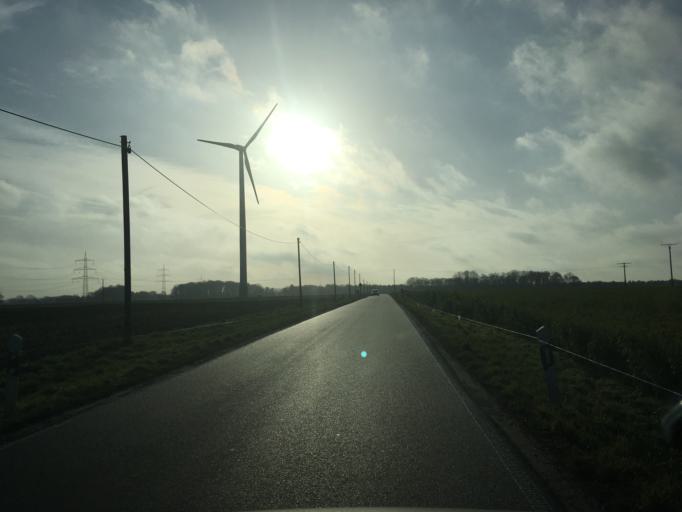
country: DE
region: North Rhine-Westphalia
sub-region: Regierungsbezirk Munster
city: Velen
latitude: 51.9291
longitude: 6.9636
